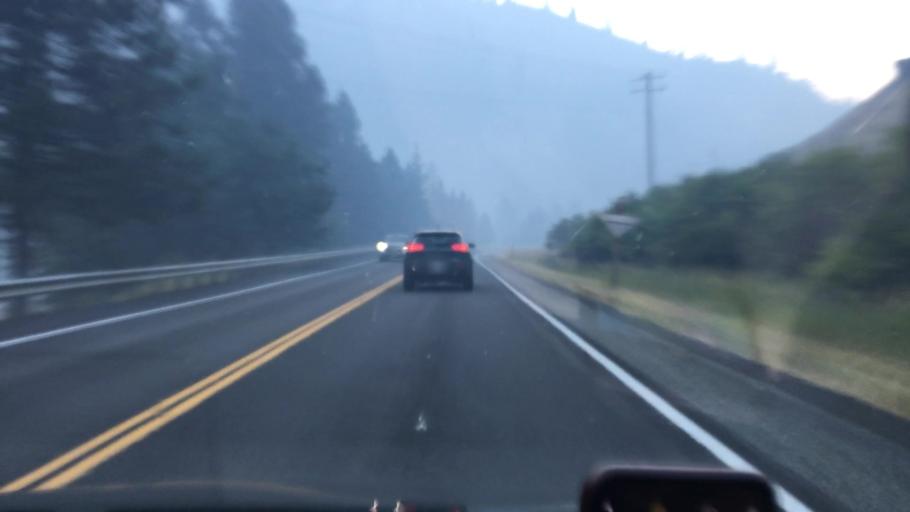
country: US
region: Idaho
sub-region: Valley County
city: McCall
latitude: 45.2692
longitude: -116.3440
